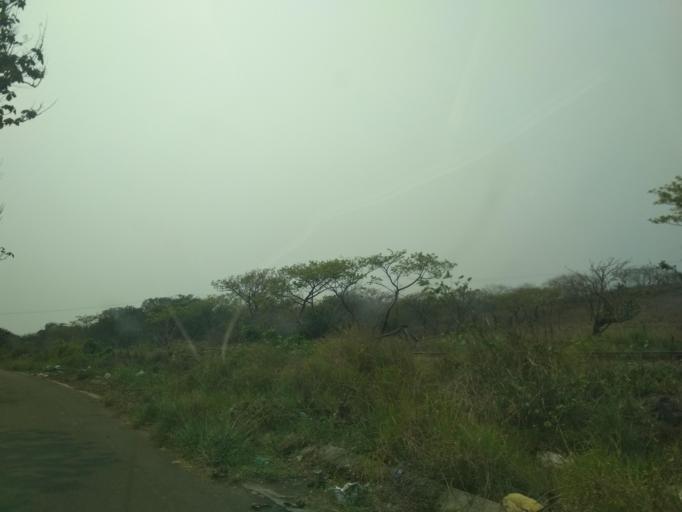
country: MX
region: Veracruz
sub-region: Veracruz
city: Delfino Victoria (Santa Fe)
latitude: 19.2171
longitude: -96.3114
